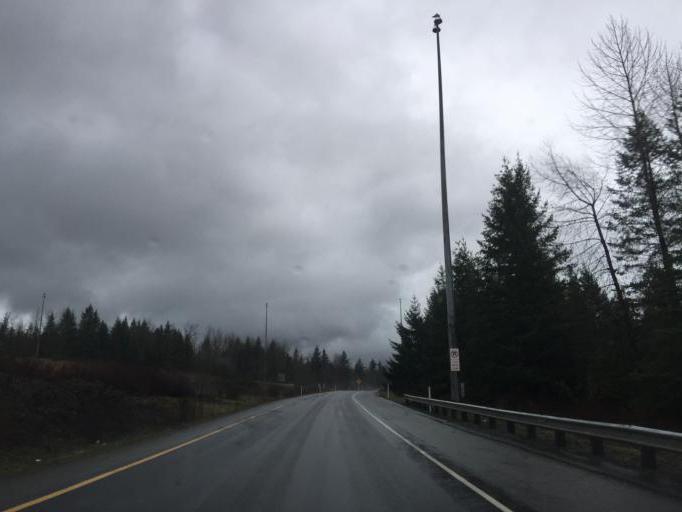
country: US
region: Washington
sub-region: King County
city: Snoqualmie
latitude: 47.5082
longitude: -121.8812
